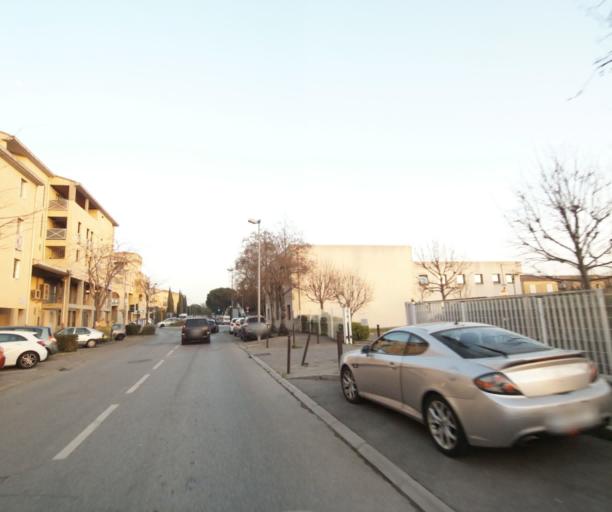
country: FR
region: Provence-Alpes-Cote d'Azur
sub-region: Departement des Bouches-du-Rhone
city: Saint-Victoret
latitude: 43.4241
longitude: 5.2706
